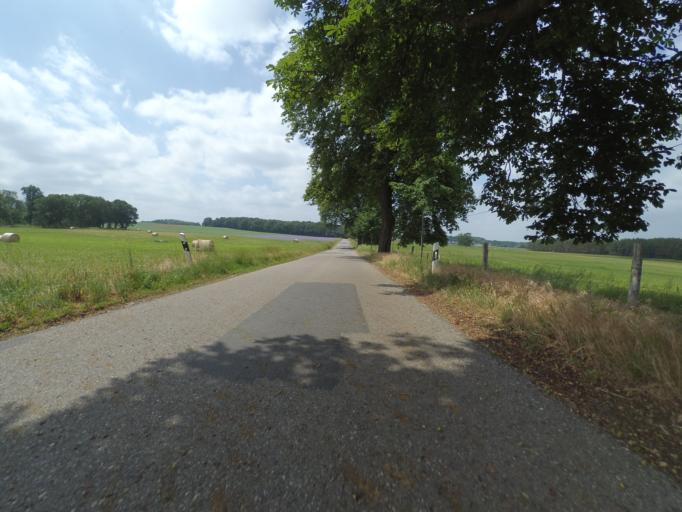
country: DE
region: Mecklenburg-Vorpommern
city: Klink
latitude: 53.4780
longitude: 12.5416
